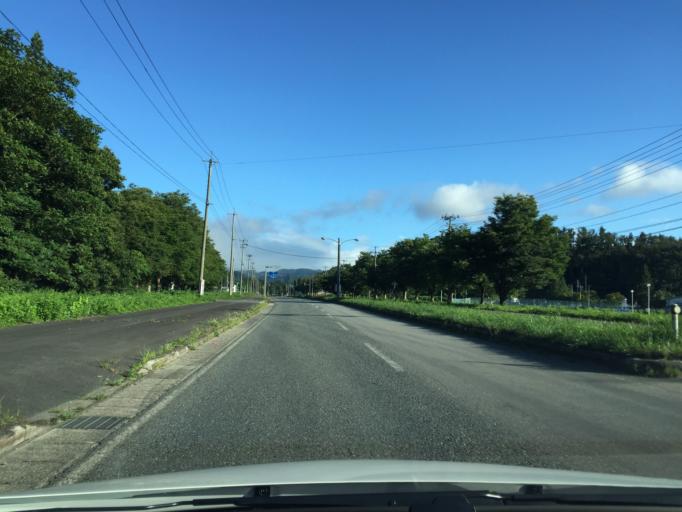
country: JP
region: Yamagata
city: Yonezawa
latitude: 37.9130
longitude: 140.1617
